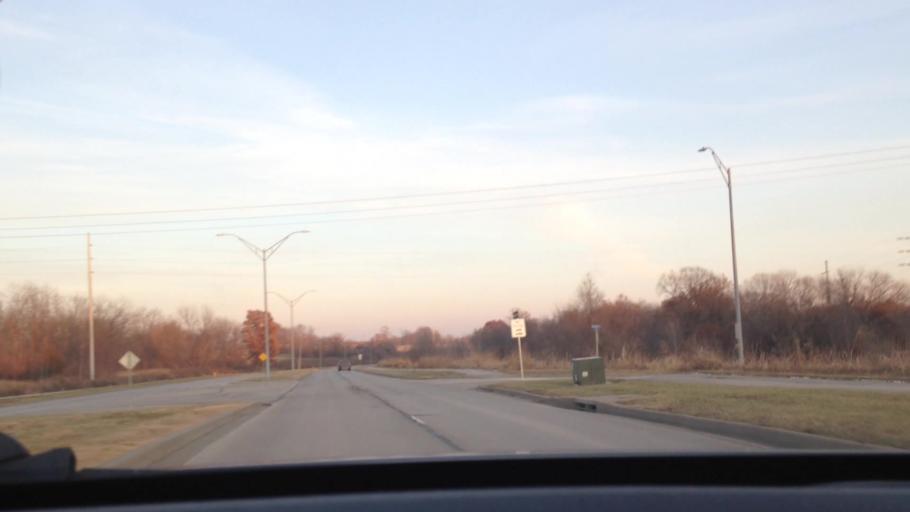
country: US
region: Missouri
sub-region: Clay County
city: Pleasant Valley
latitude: 39.2097
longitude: -94.4585
